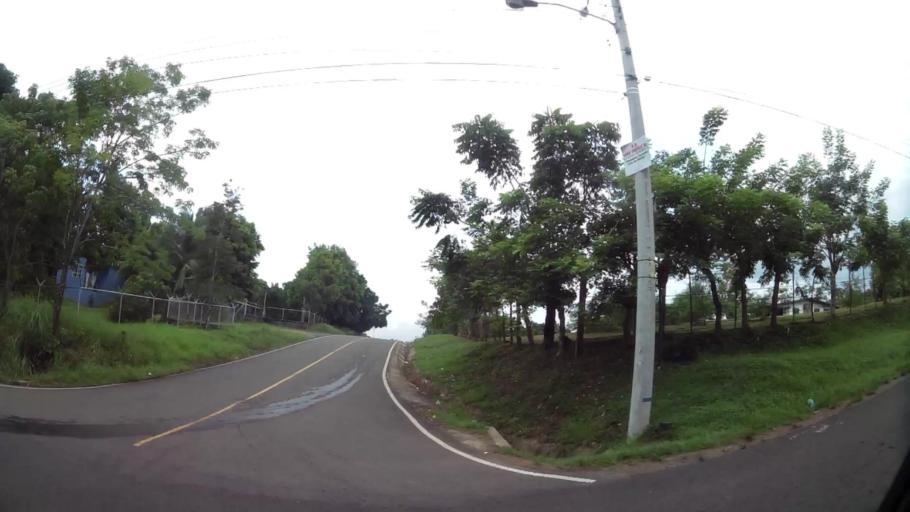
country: PA
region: Panama
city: Cabra Numero Uno
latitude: 9.1233
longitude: -79.3617
